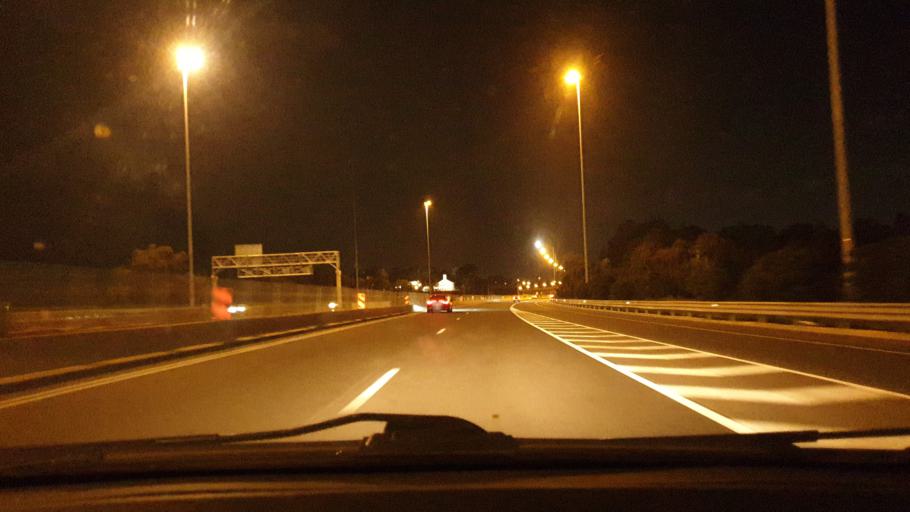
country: IL
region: Central District
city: Ramla
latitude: 31.9232
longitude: 34.8356
